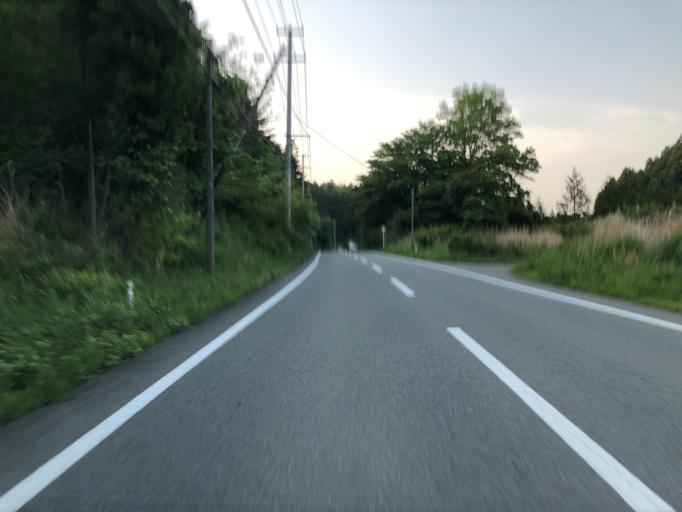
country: JP
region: Fukushima
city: Namie
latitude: 37.2644
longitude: 140.9739
